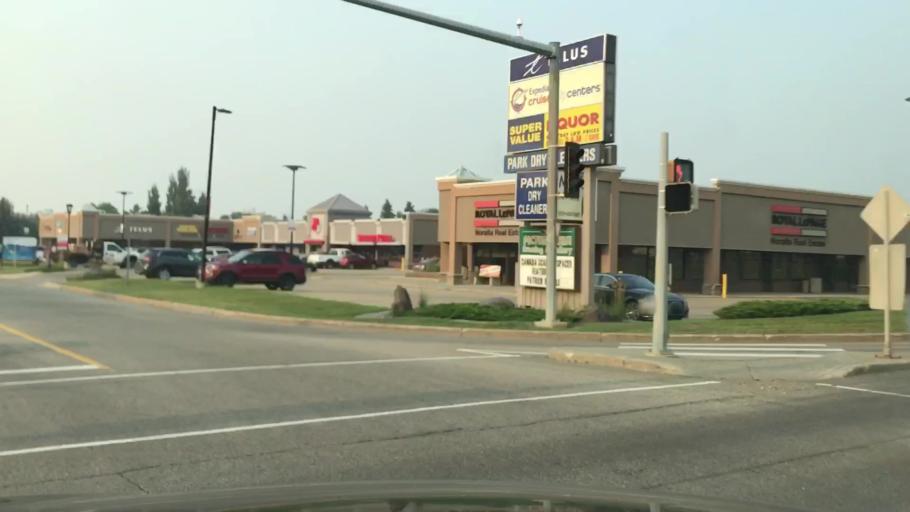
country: CA
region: Alberta
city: Sherwood Park
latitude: 53.5122
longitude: -113.3303
